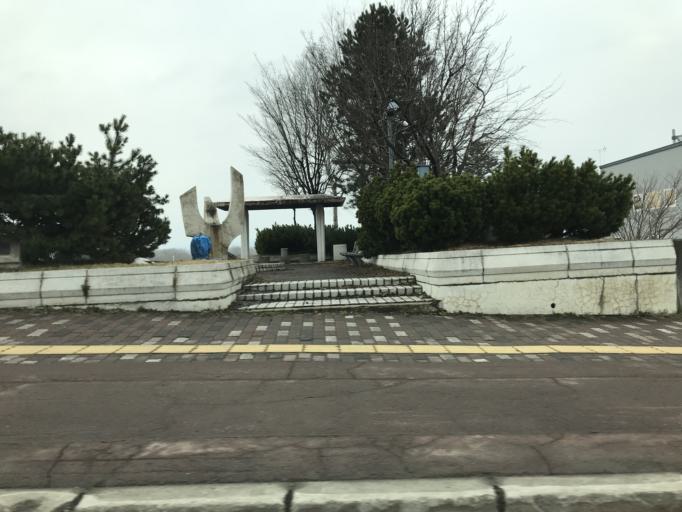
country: JP
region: Hokkaido
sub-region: Asahikawa-shi
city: Asahikawa
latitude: 43.7658
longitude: 142.3486
